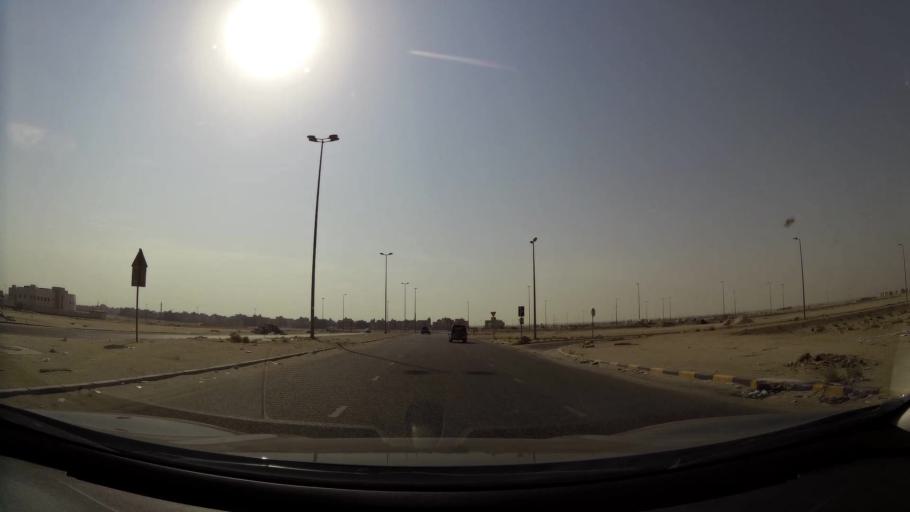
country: KW
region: Al Ahmadi
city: Al Wafrah
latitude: 28.7812
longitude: 48.0517
